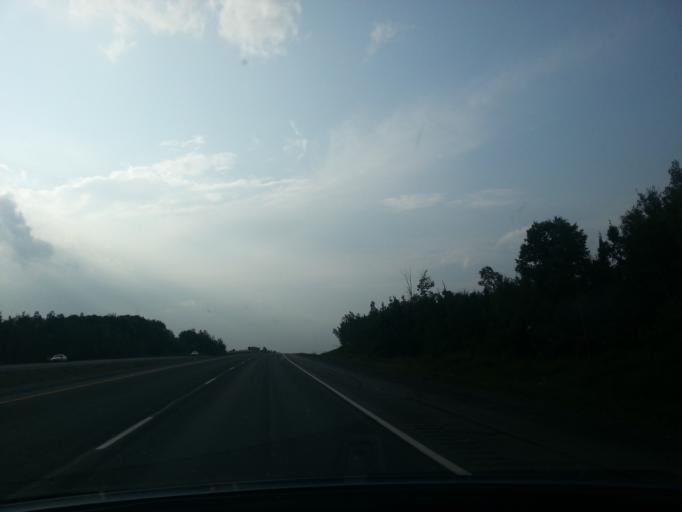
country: CA
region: New Brunswick
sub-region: Madawaska County
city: Saint-Leonard
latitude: 47.1193
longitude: -67.8469
